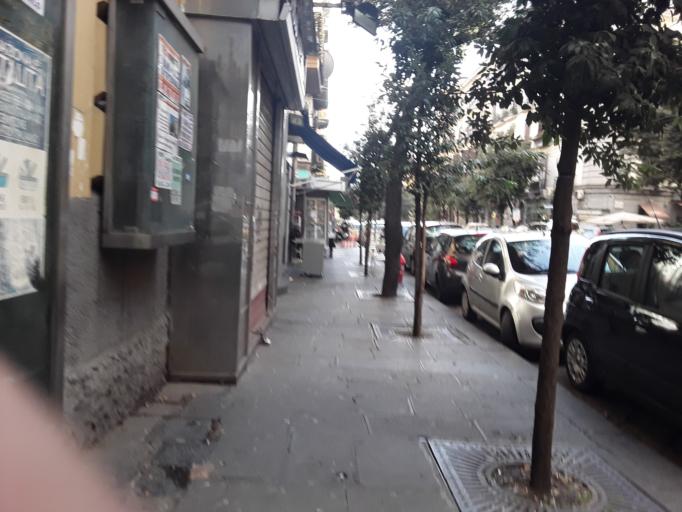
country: IT
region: Campania
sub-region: Provincia di Napoli
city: Napoli
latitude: 40.8589
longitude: 14.2669
